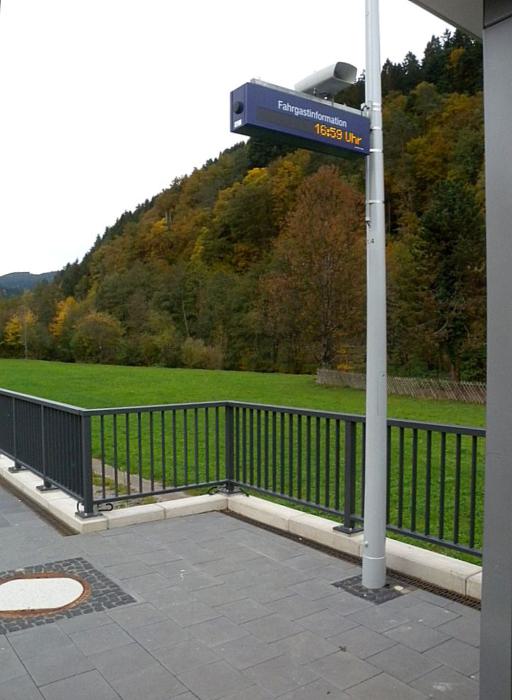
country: DE
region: Baden-Wuerttemberg
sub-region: Freiburg Region
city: Hausach
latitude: 48.2720
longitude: 8.1985
